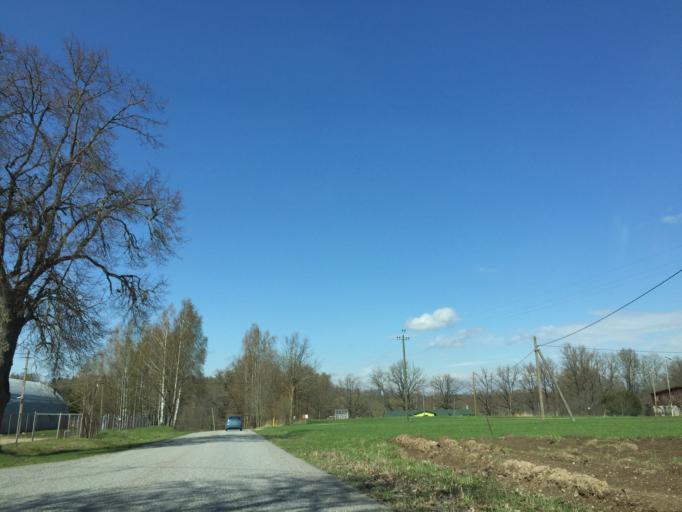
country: EE
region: Tartu
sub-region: Elva linn
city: Elva
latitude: 58.1498
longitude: 26.2325
